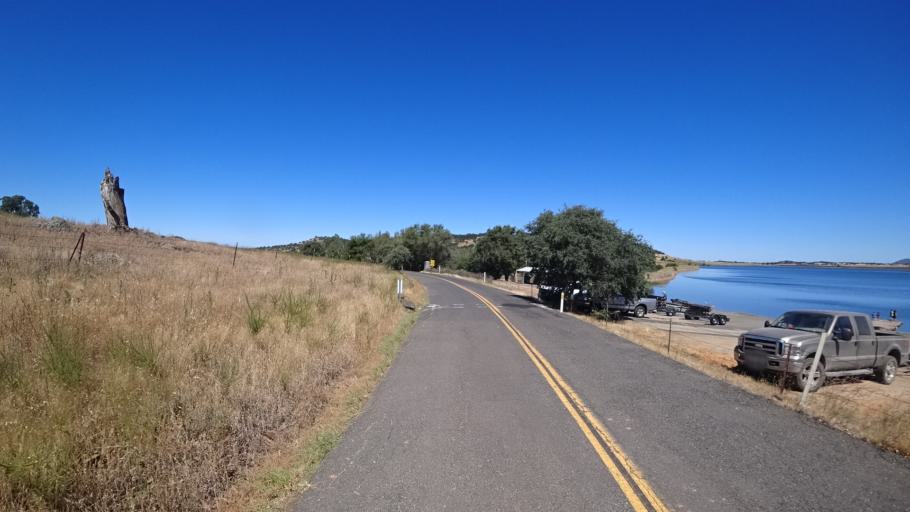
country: US
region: California
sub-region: Calaveras County
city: Copperopolis
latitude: 38.0255
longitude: -120.7600
